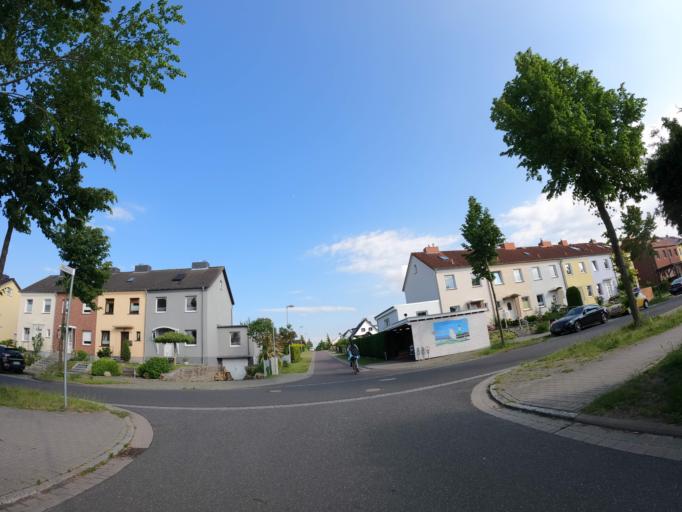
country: DE
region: Mecklenburg-Vorpommern
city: Stralsund
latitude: 54.2969
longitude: 13.0667
